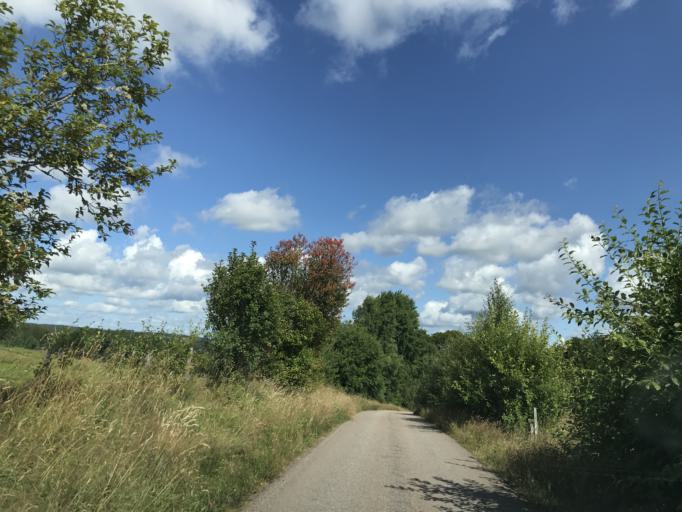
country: SE
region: Halland
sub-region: Laholms Kommun
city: Knared
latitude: 56.5136
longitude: 13.3019
